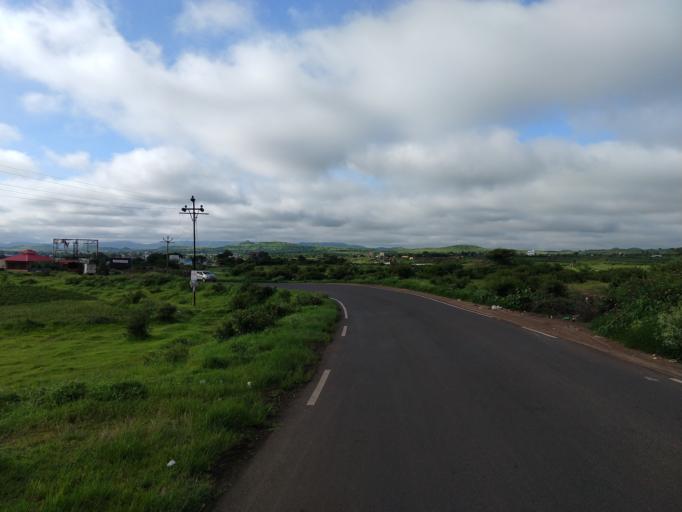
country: IN
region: Maharashtra
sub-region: Pune Division
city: Khed
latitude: 18.3997
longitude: 73.9126
